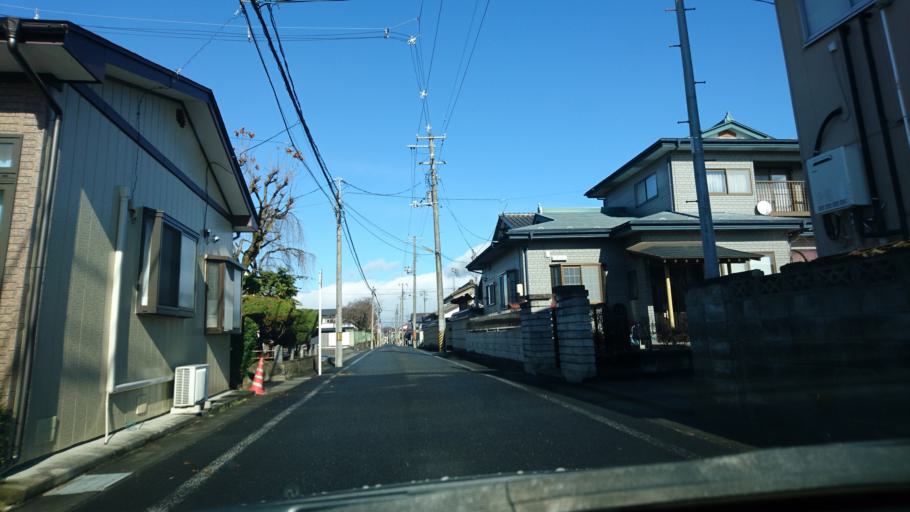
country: JP
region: Iwate
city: Ichinoseki
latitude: 38.9373
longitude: 141.1273
